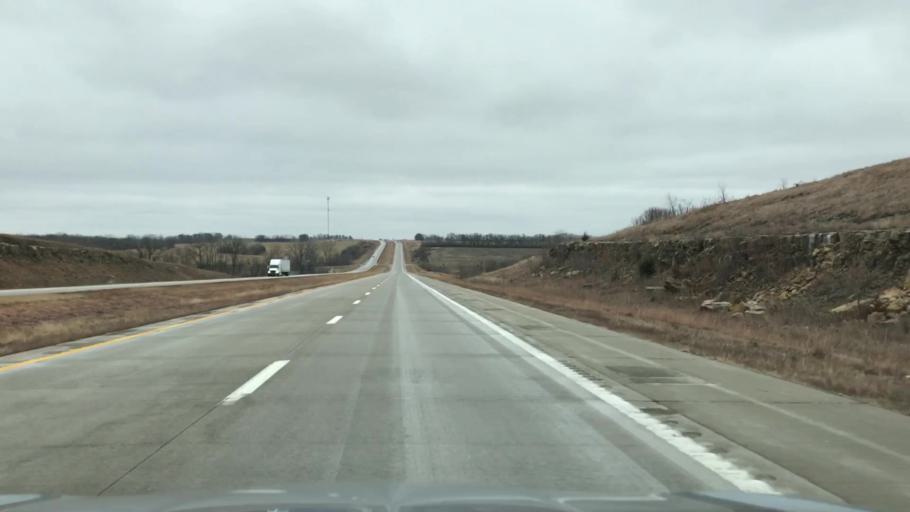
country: US
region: Missouri
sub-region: Caldwell County
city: Hamilton
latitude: 39.7348
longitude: -93.7862
